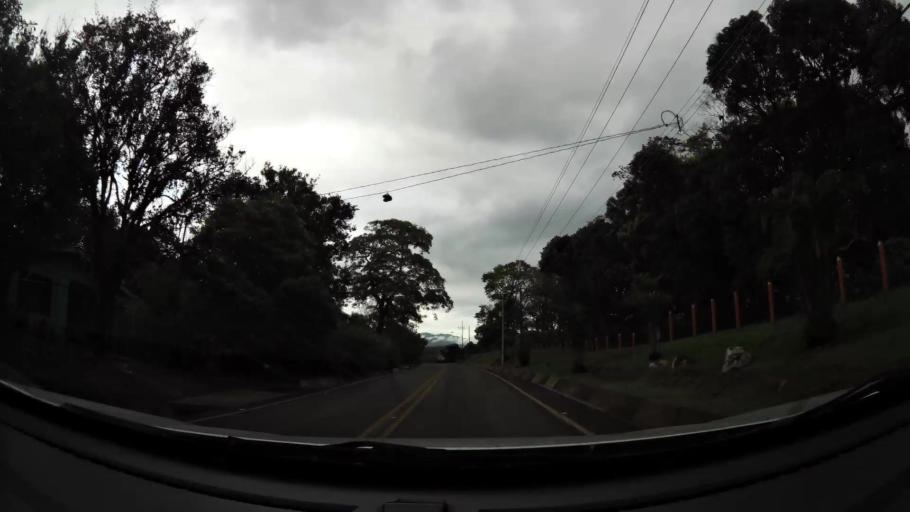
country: CR
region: Alajuela
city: Orotina
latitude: 9.9549
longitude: -84.5791
